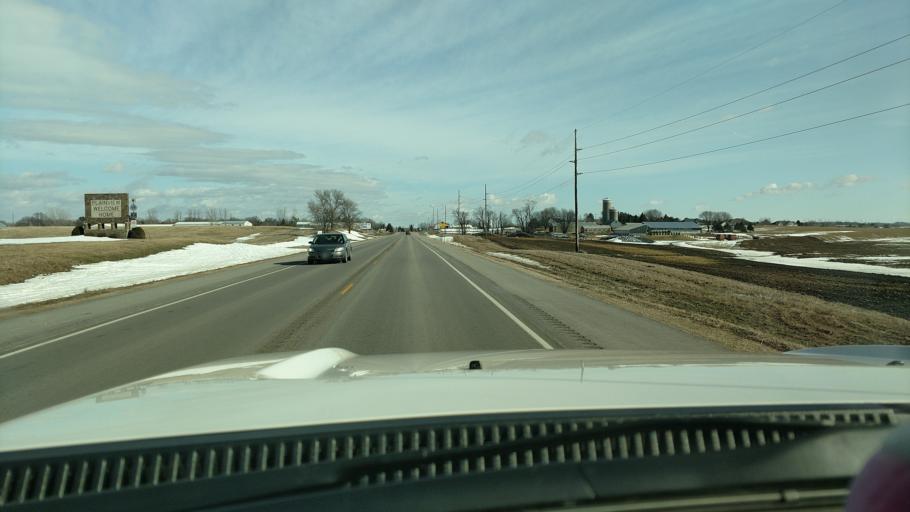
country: US
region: Minnesota
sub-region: Wabasha County
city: Plainview
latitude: 44.1580
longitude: -92.1866
